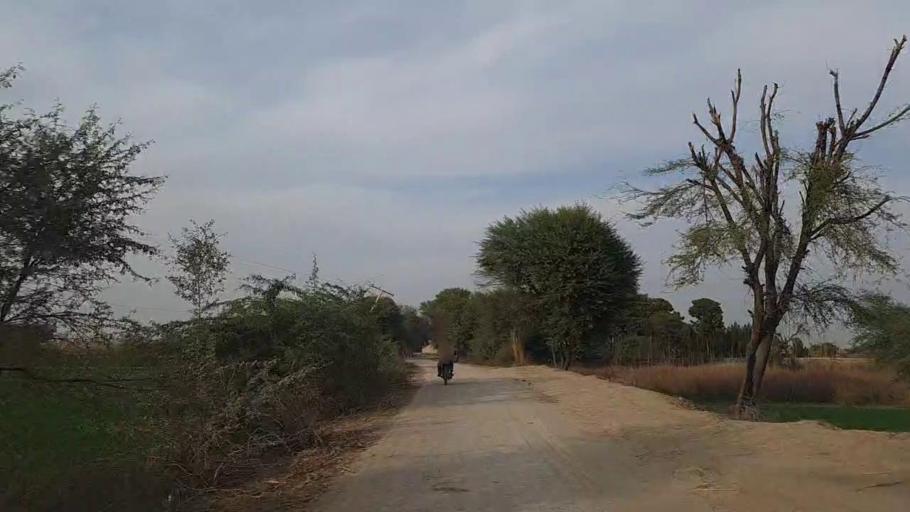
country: PK
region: Sindh
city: Daur
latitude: 26.5129
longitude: 68.4434
